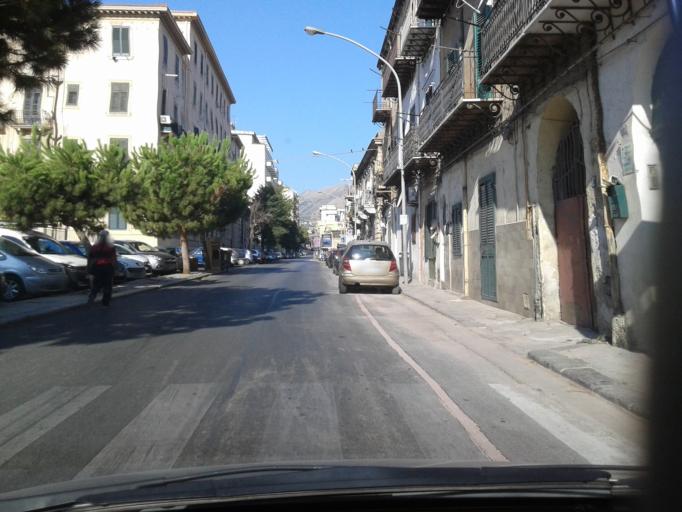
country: IT
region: Sicily
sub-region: Palermo
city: Palermo
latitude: 38.1108
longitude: 13.3451
